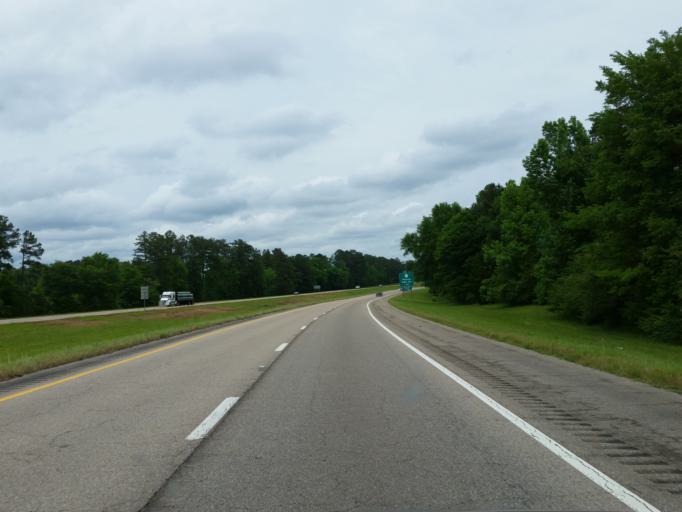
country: US
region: Mississippi
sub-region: Clarke County
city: Stonewall
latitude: 32.0459
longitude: -88.9187
